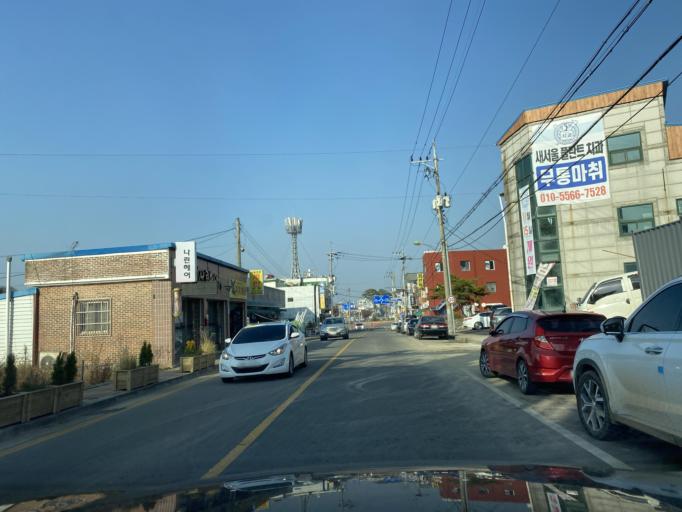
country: KR
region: Chungcheongnam-do
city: Yesan
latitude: 36.6846
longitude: 126.8293
